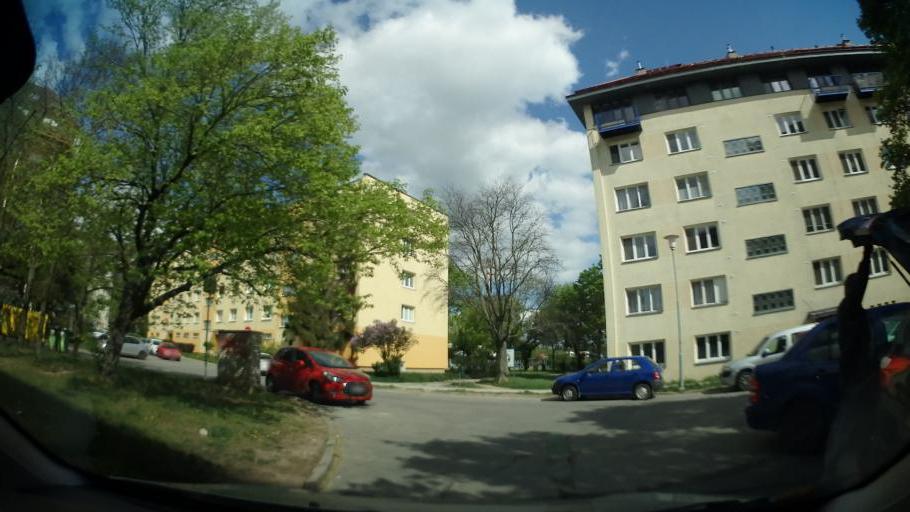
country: CZ
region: South Moravian
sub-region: Mesto Brno
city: Brno
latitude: 49.1893
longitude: 16.6599
